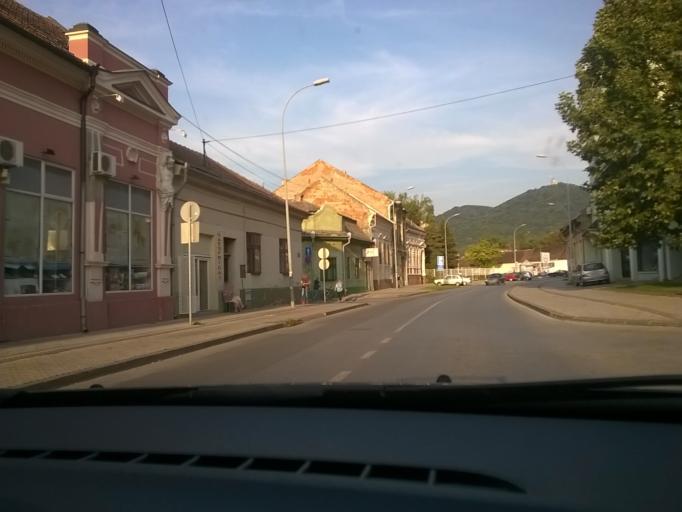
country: RS
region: Autonomna Pokrajina Vojvodina
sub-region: Juznobanatski Okrug
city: Vrsac
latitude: 45.1224
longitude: 21.2987
